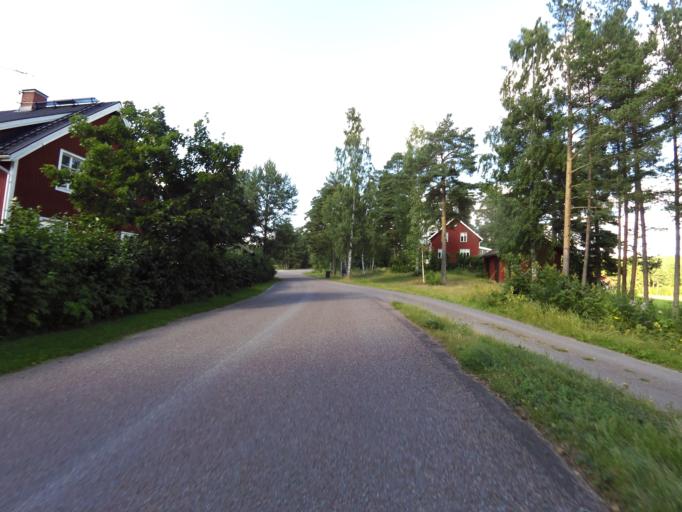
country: SE
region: Dalarna
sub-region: Faluns Kommun
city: Svardsjo
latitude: 60.6610
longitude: 15.8419
